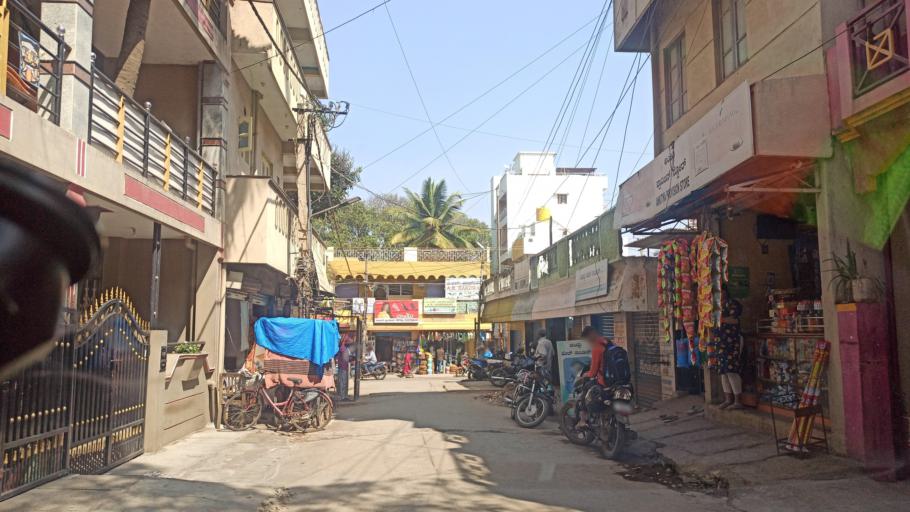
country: IN
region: Karnataka
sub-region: Bangalore Urban
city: Yelahanka
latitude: 13.0394
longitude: 77.5943
